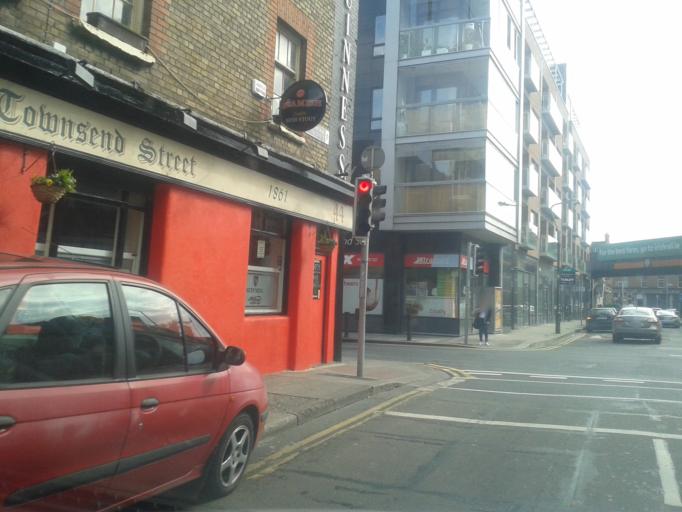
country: IE
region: Leinster
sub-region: Dublin City
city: Dublin
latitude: 53.3459
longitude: -6.2520
